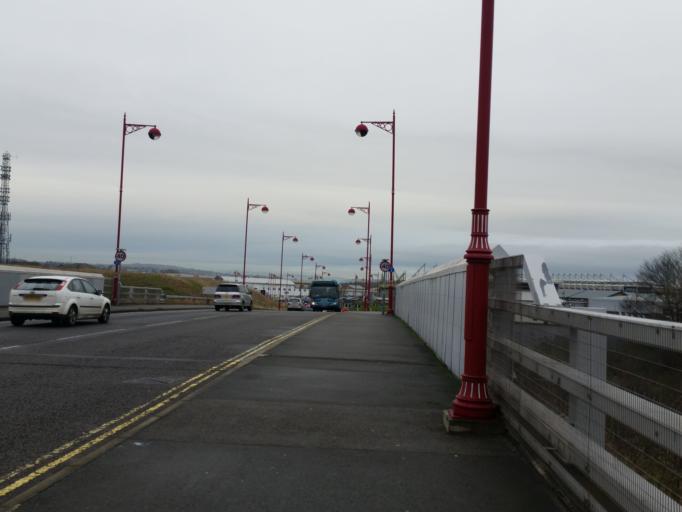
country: GB
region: England
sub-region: Derby
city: Derby
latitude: 52.9090
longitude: -1.4486
